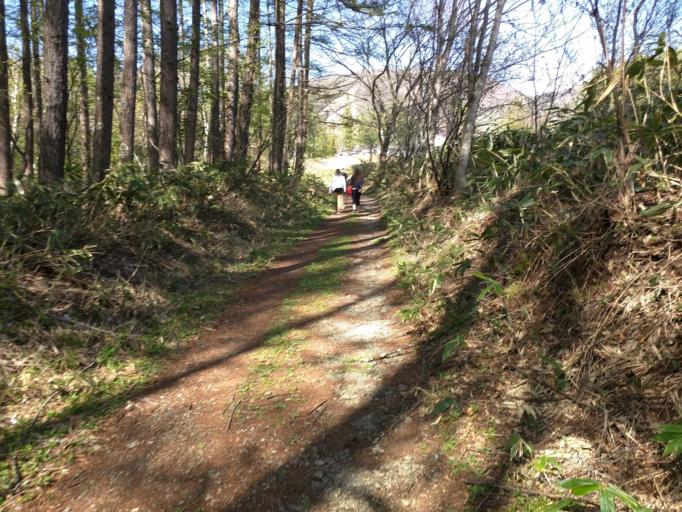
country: JP
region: Nagano
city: Nagano-shi
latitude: 36.7361
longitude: 138.0819
